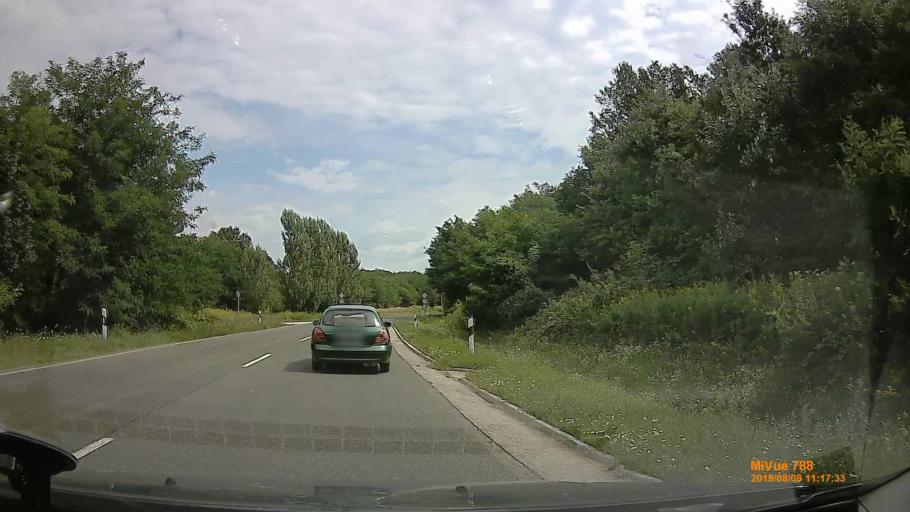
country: HU
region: Somogy
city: Balatonbereny
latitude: 46.6599
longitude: 17.3182
